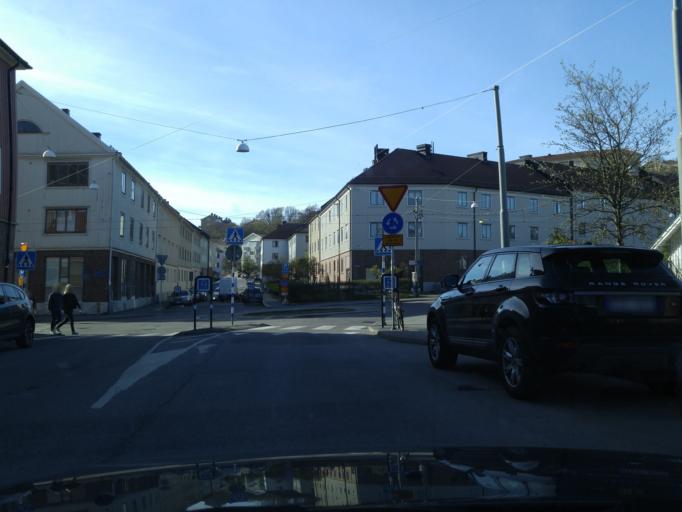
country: SE
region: Vaestra Goetaland
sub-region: Goteborg
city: Majorna
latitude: 57.6856
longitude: 11.9278
